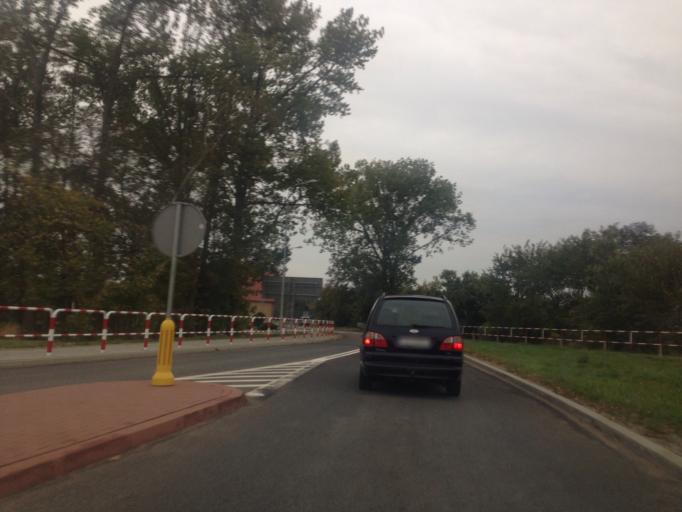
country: PL
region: Greater Poland Voivodeship
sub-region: Powiat gnieznienski
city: Lubowo
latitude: 52.4894
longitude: 17.4283
